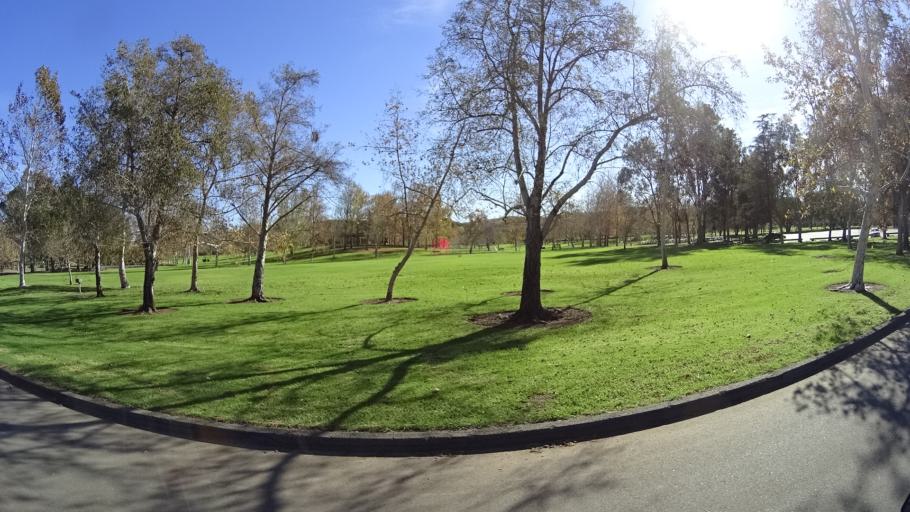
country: US
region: California
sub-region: Orange County
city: North Tustin
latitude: 33.7997
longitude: -117.7579
